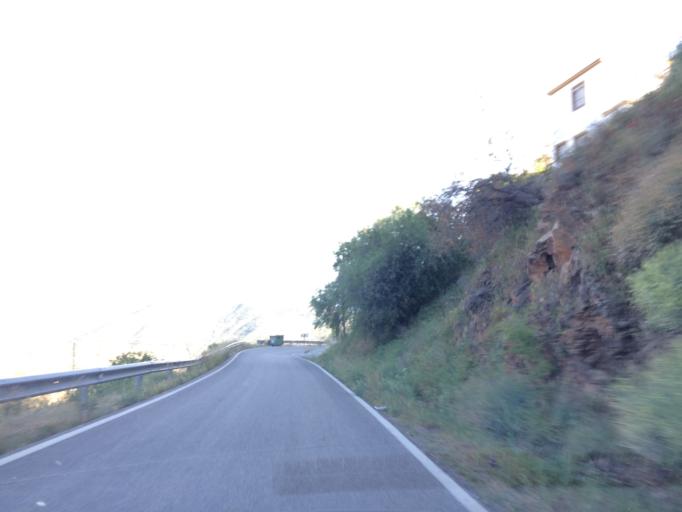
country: ES
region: Andalusia
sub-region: Provincia de Malaga
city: Totalan
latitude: 36.7737
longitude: -4.3196
